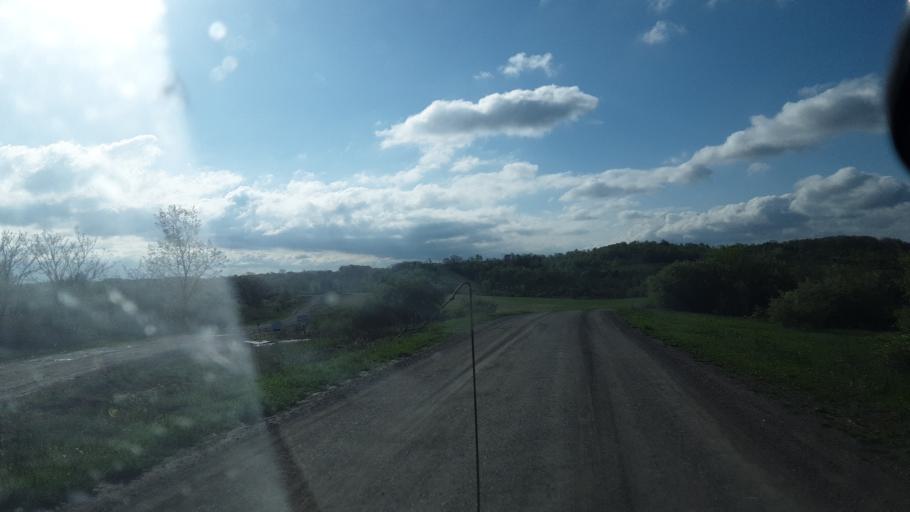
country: US
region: Ohio
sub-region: Noble County
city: Caldwell
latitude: 39.8008
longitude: -81.6368
